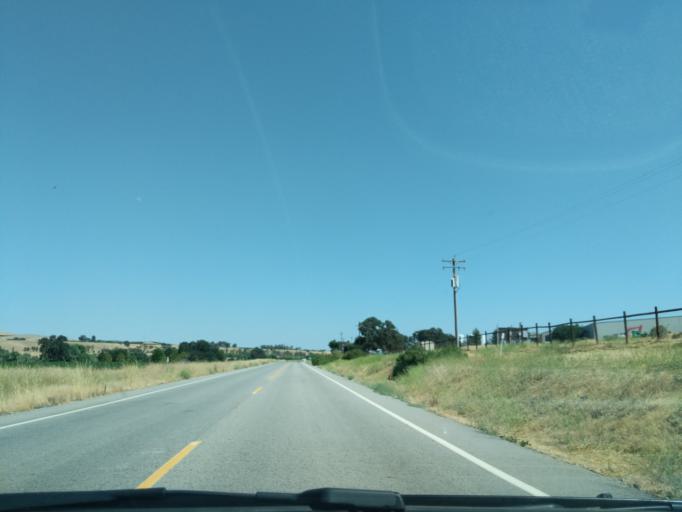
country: US
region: California
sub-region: San Luis Obispo County
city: San Miguel
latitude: 35.7670
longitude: -120.6998
